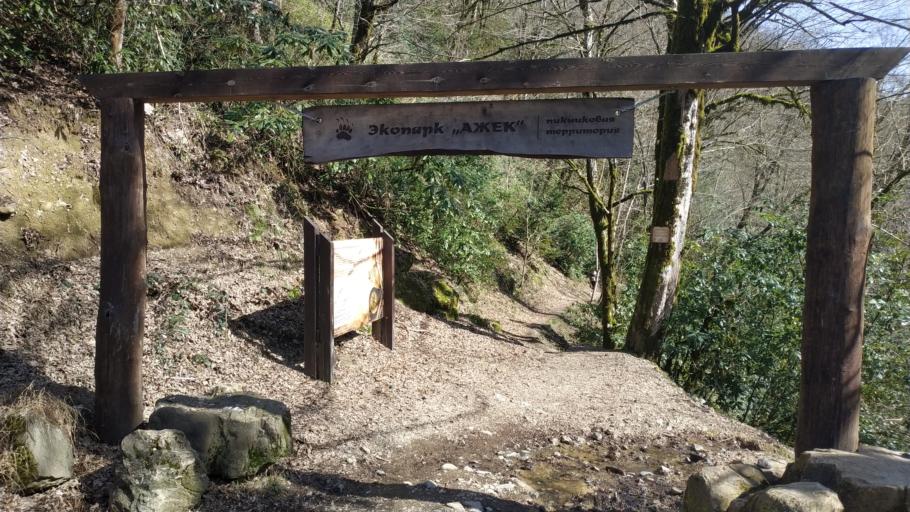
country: RU
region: Krasnodarskiy
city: Dagomys
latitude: 43.7082
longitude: 39.7802
